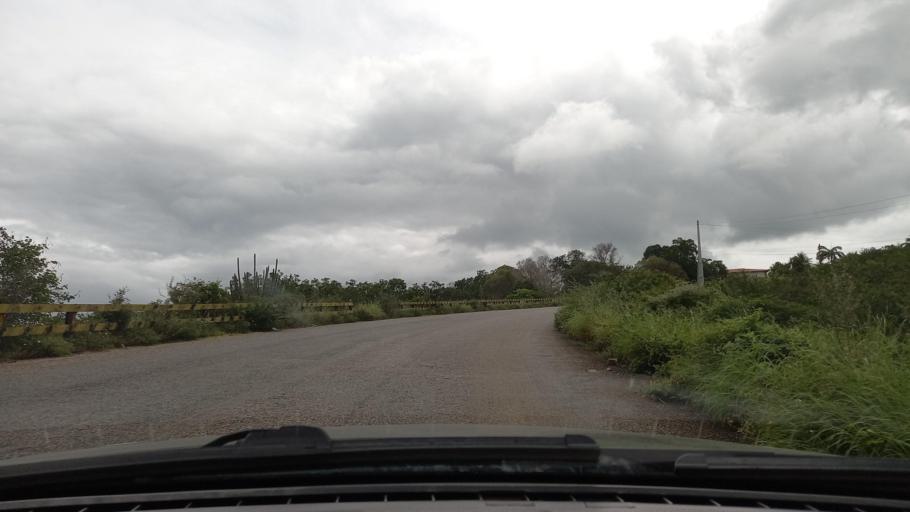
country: BR
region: Sergipe
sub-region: Caninde De Sao Francisco
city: Caninde de Sao Francisco
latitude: -9.6313
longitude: -37.7845
